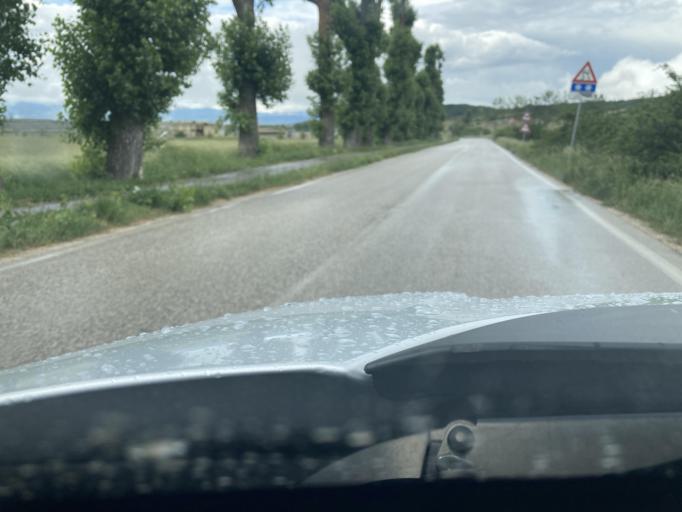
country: IT
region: Abruzzo
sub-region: Provincia dell' Aquila
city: Rocca di Mezzo
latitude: 42.2142
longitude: 13.5282
